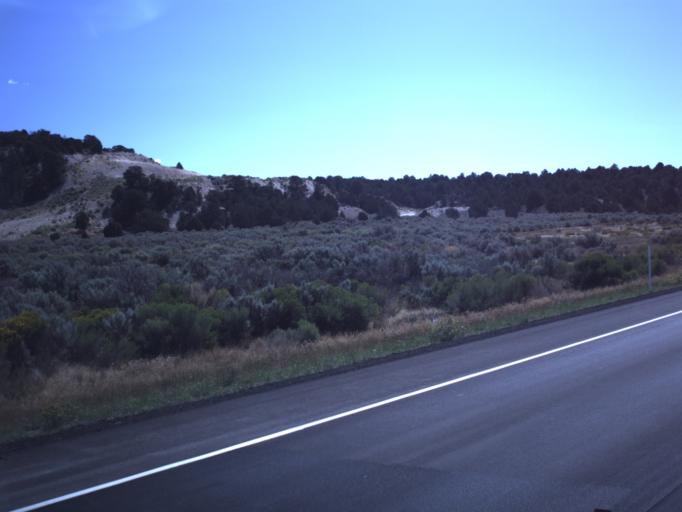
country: US
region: Utah
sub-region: Utah County
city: Eagle Mountain
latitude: 39.9867
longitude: -112.2646
